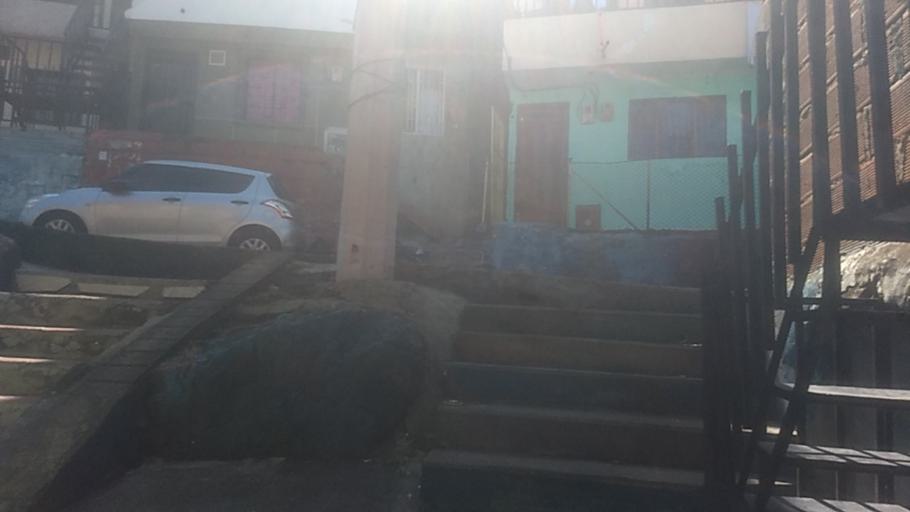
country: CO
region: Antioquia
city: Bello
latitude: 6.2966
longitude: -75.5493
